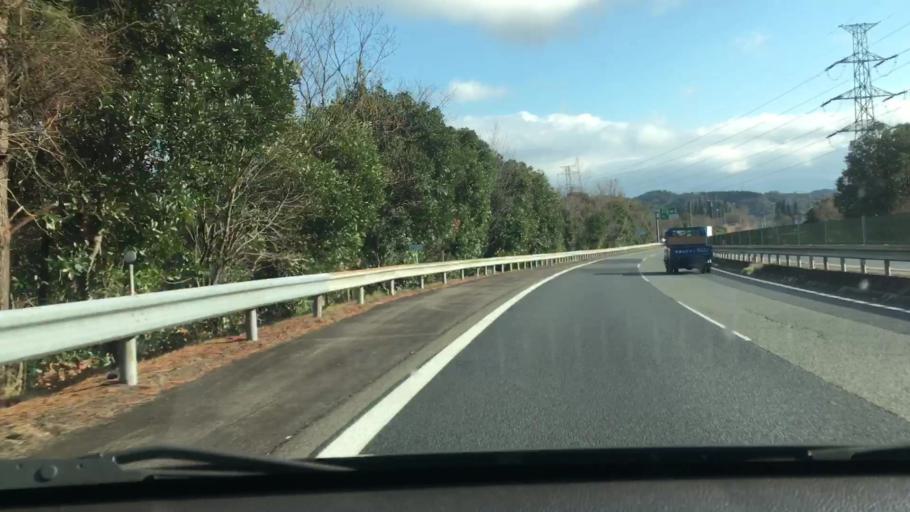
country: JP
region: Kumamoto
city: Hitoyoshi
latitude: 32.2655
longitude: 130.7657
